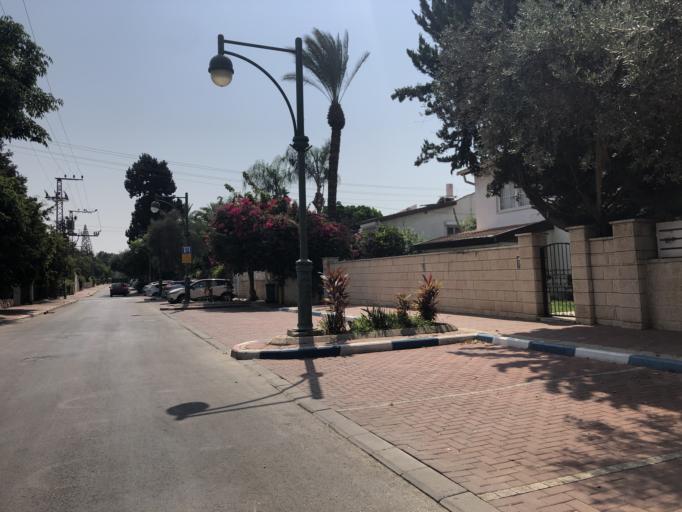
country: IL
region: Tel Aviv
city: Giv`atayim
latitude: 32.0543
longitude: 34.8318
